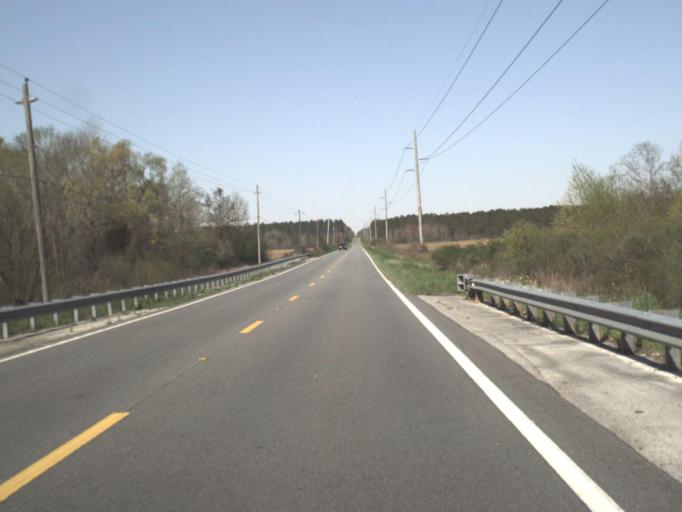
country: US
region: Florida
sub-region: Jackson County
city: Graceville
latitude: 30.9537
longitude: -85.4597
